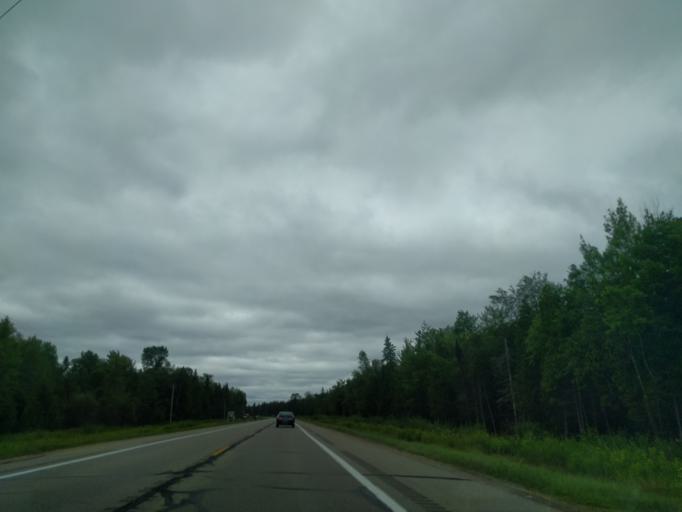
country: US
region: Michigan
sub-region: Delta County
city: Escanaba
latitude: 45.6514
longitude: -87.1813
